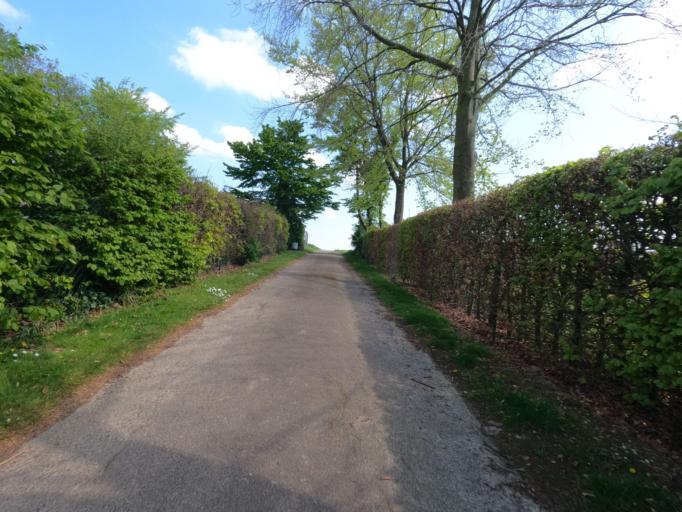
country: DE
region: North Rhine-Westphalia
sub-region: Regierungsbezirk Koln
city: Heinsberg
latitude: 51.0534
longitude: 6.0760
